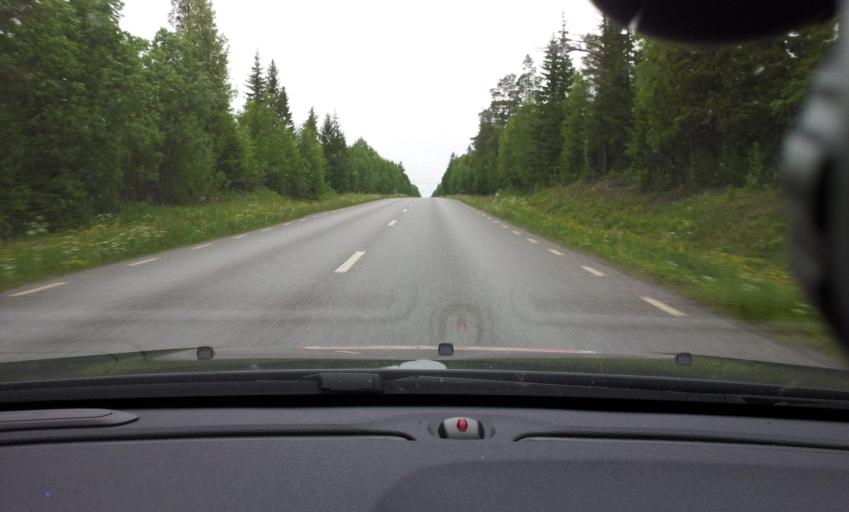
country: SE
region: Jaemtland
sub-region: Krokoms Kommun
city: Valla
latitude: 63.2199
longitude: 14.0221
